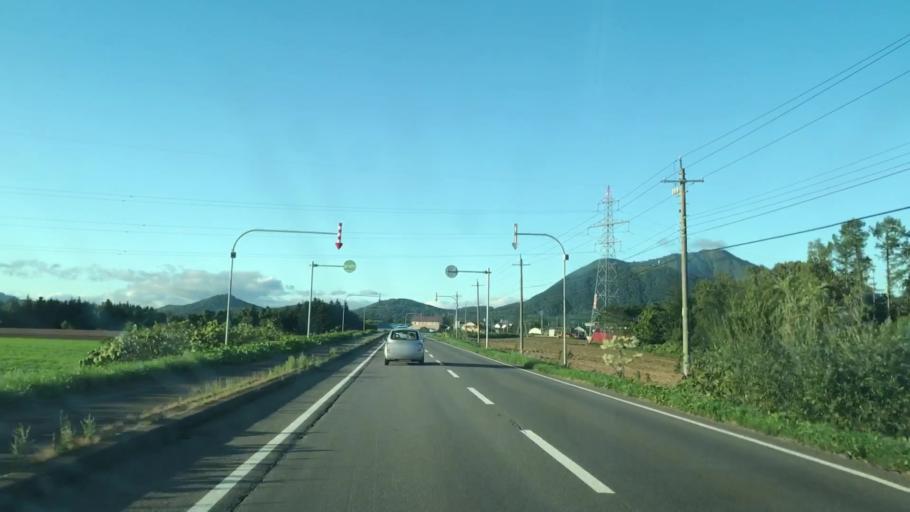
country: JP
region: Hokkaido
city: Niseko Town
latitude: 42.7195
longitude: 140.8602
